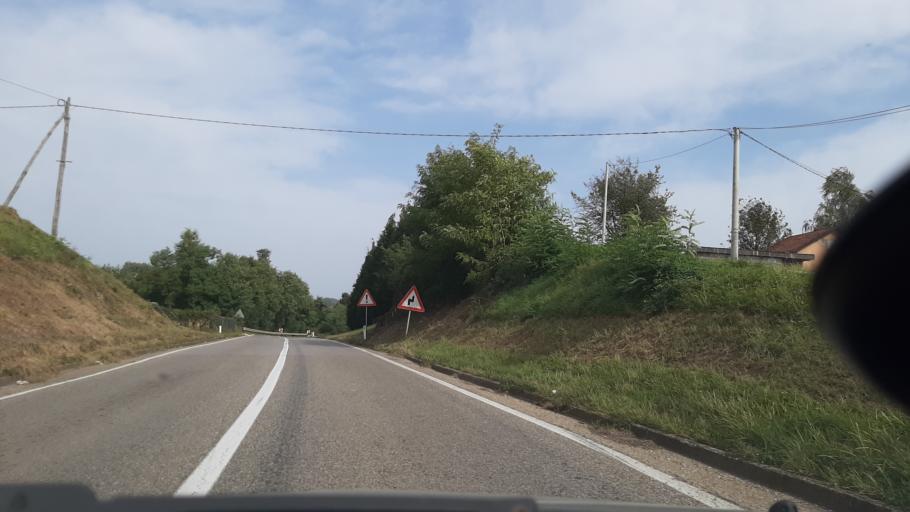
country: BA
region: Republika Srpska
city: Laktasi
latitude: 44.8724
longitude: 17.3563
